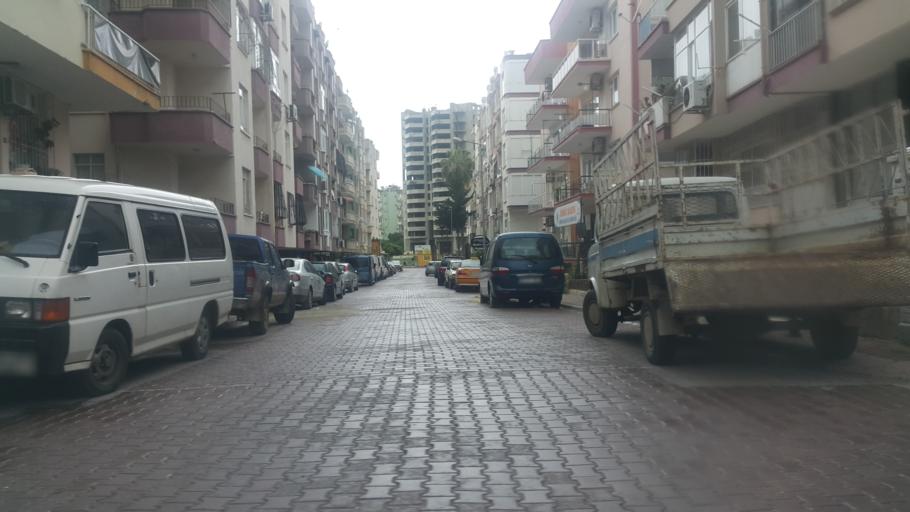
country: TR
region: Mersin
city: Mercin
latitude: 36.7801
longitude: 34.5920
